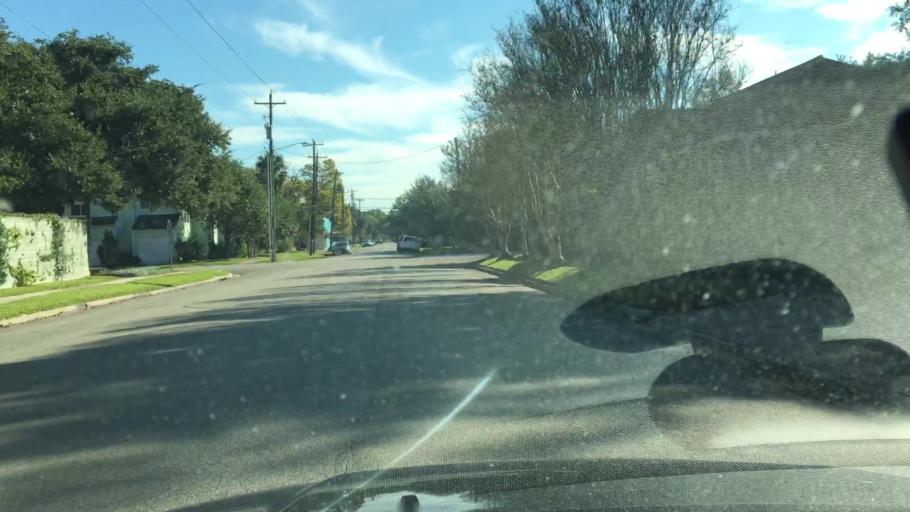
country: US
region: Texas
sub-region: Harris County
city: Houston
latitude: 29.7980
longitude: -95.4008
